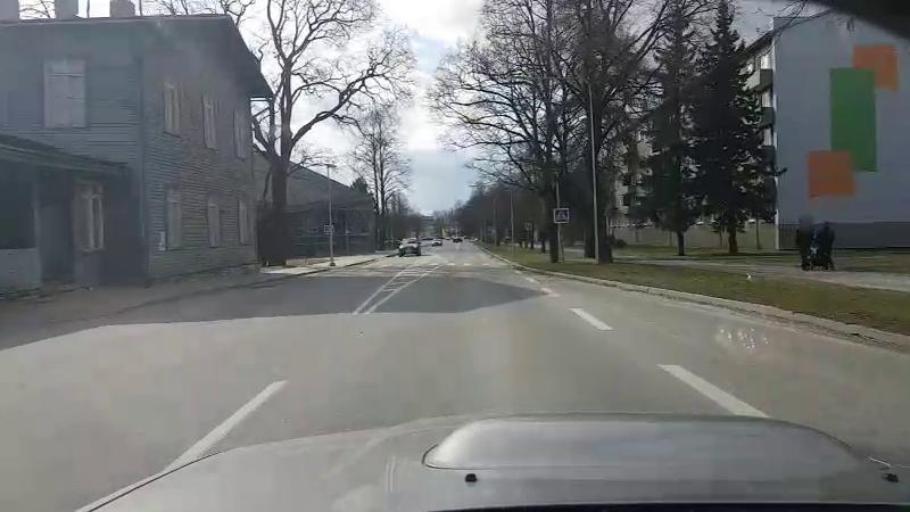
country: EE
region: Jaervamaa
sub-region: Paide linn
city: Paide
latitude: 58.8867
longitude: 25.5665
